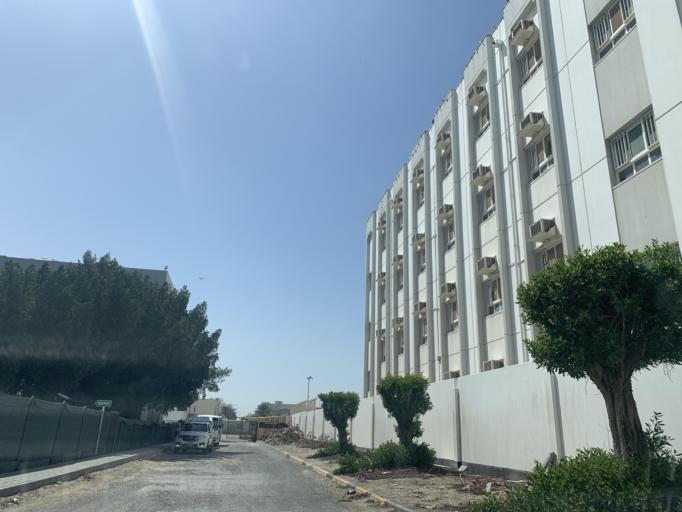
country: BH
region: Manama
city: Manama
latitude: 26.2071
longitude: 50.5731
